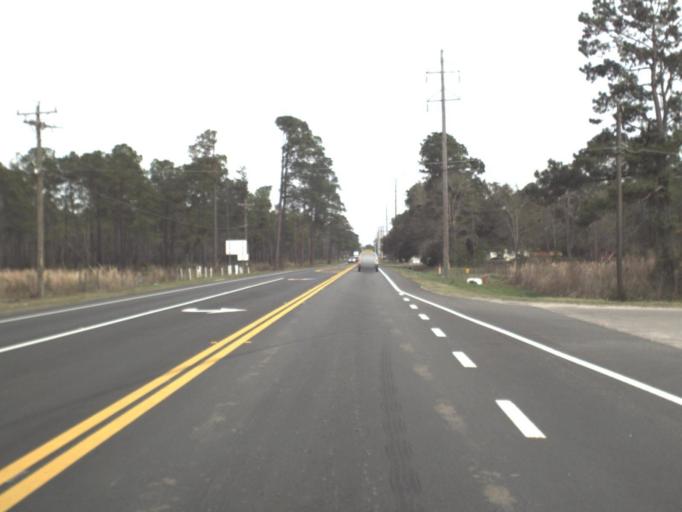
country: US
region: Florida
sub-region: Gadsden County
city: Midway
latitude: 30.4430
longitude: -84.4116
